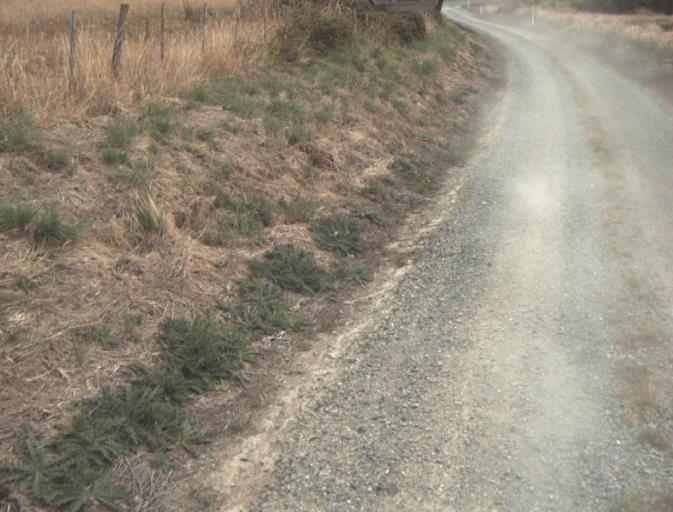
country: AU
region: Tasmania
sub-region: Launceston
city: Mayfield
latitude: -41.2104
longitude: 147.1093
